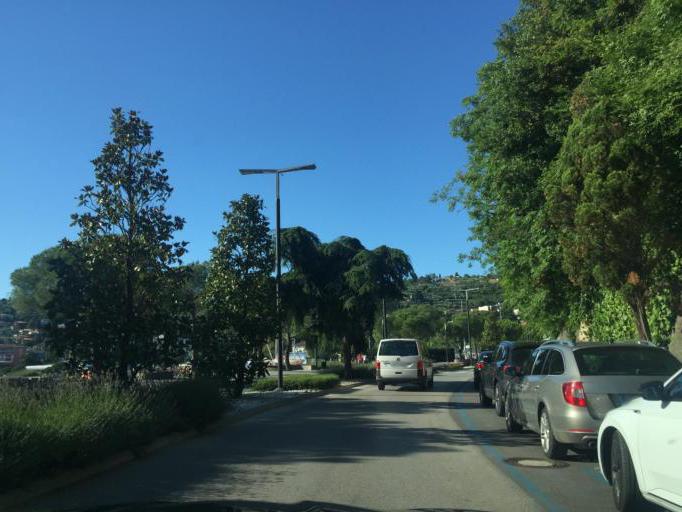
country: SI
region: Piran-Pirano
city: Portoroz
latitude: 45.5099
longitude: 13.5942
